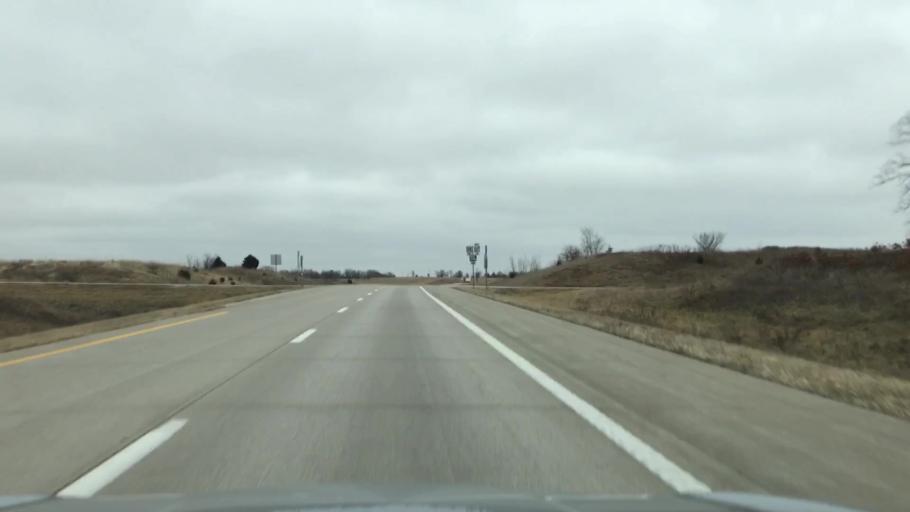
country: US
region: Missouri
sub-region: Linn County
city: Marceline
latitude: 39.7635
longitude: -92.7919
